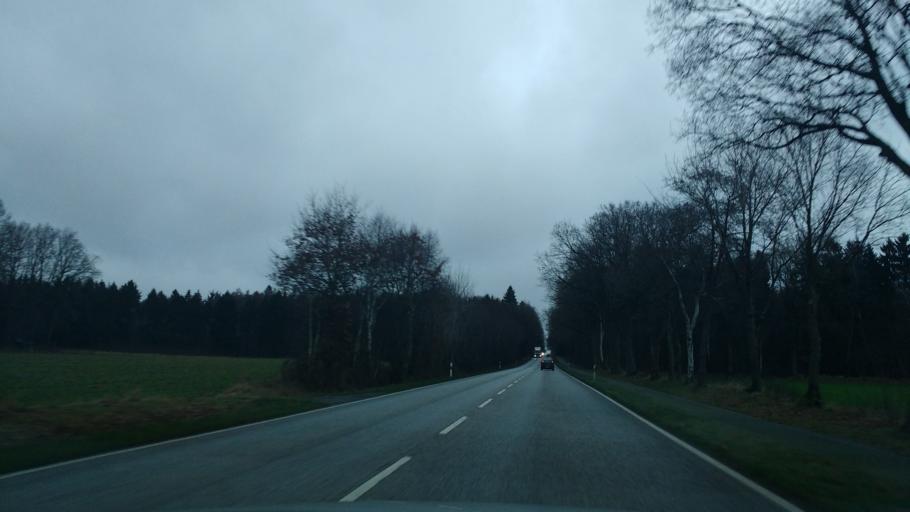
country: DE
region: Schleswig-Holstein
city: Peissen
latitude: 54.0053
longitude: 9.5873
